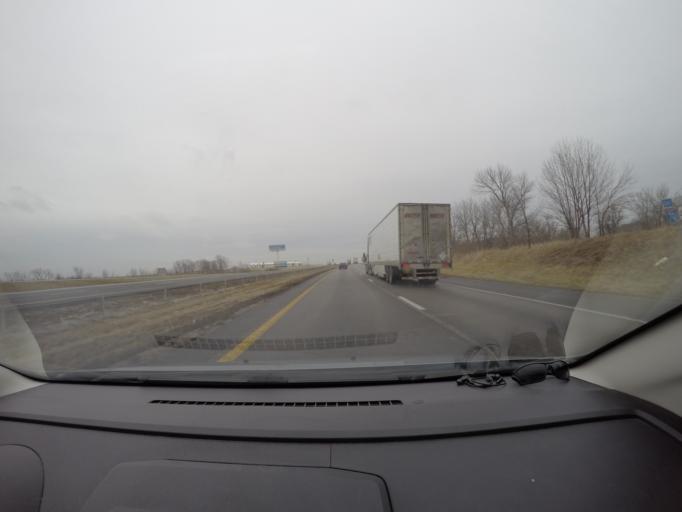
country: US
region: Missouri
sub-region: Warren County
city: Warrenton
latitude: 38.8558
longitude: -91.2973
